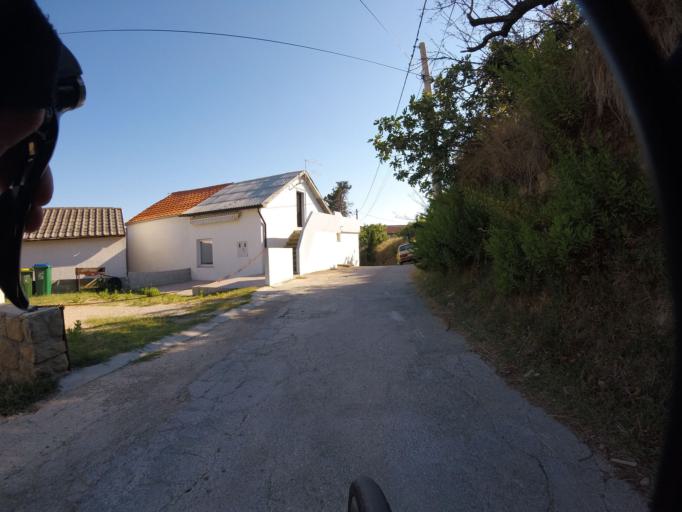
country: HR
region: Primorsko-Goranska
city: Lopar
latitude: 44.8373
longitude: 14.7380
